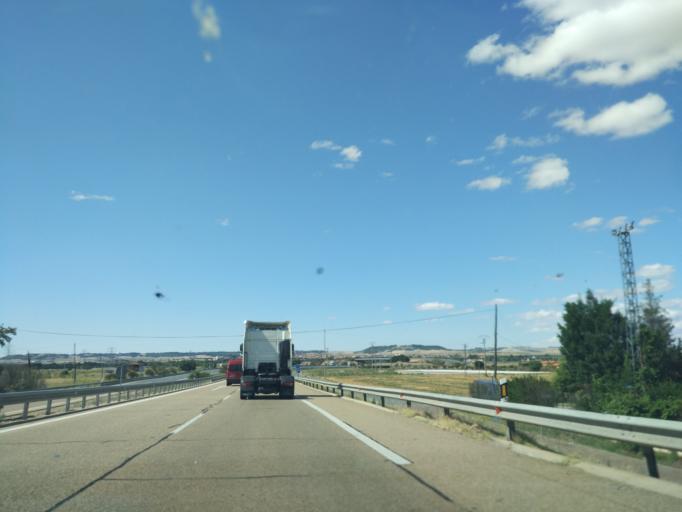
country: ES
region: Castille and Leon
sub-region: Provincia de Valladolid
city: Tordesillas
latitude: 41.4737
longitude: -4.9895
